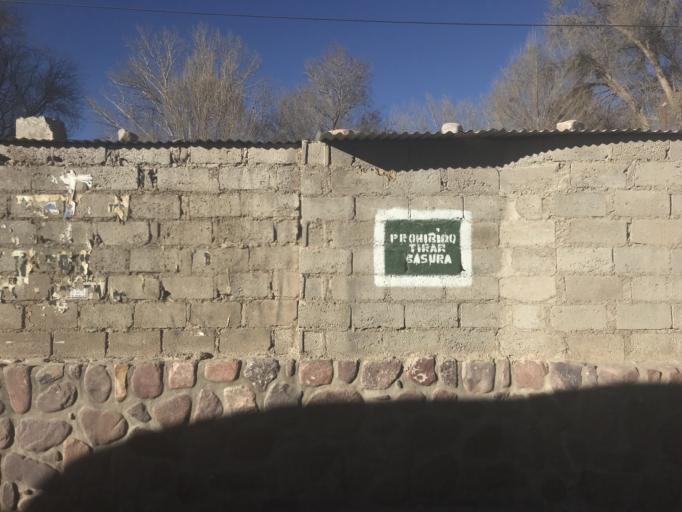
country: AR
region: Jujuy
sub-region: Departamento de Humahuaca
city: Humahuaca
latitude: -23.2031
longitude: -65.3473
